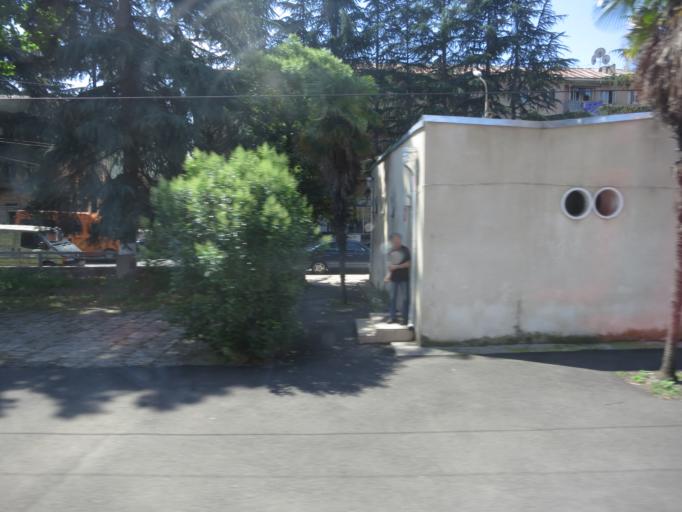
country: GE
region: Imereti
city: Zestap'oni
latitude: 42.1080
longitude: 43.0402
